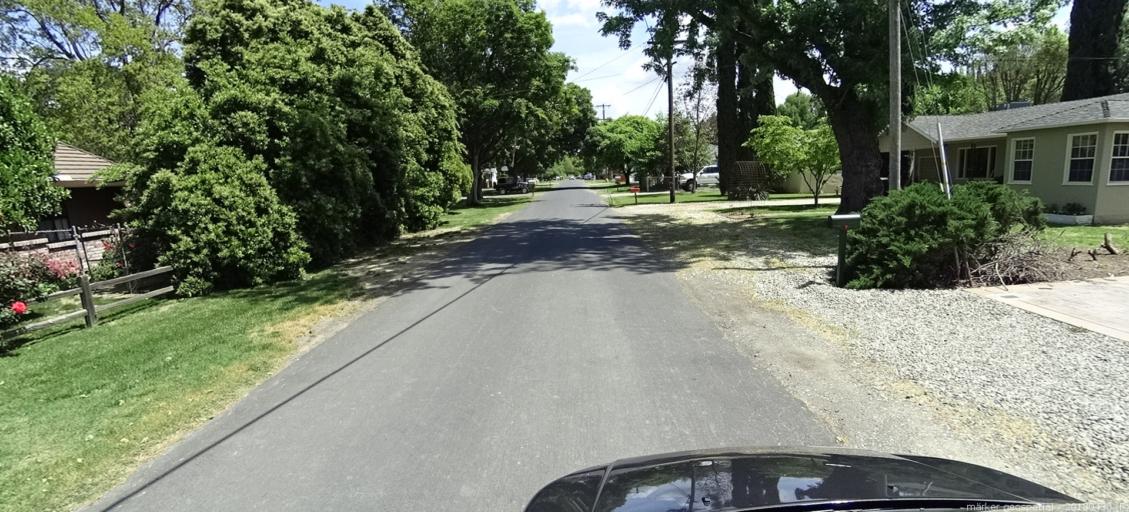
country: US
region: California
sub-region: Yolo County
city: West Sacramento
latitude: 38.5407
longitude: -121.5273
